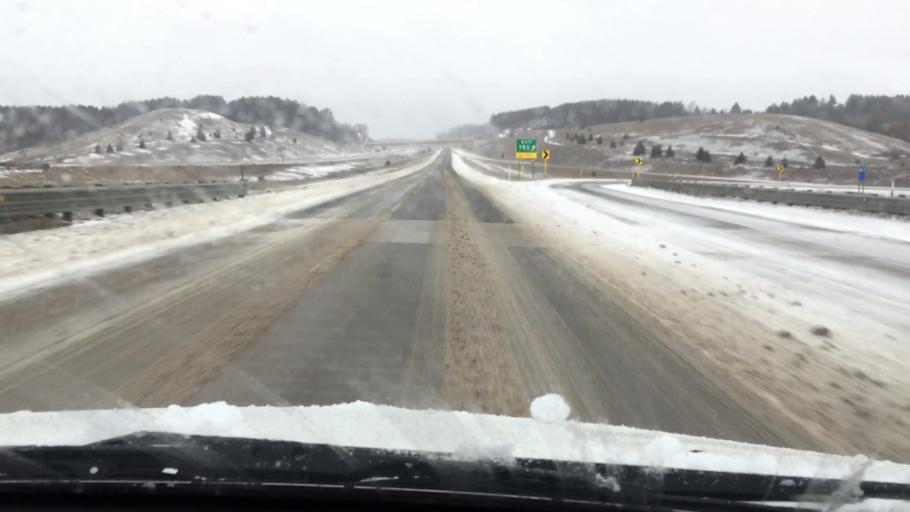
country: US
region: Michigan
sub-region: Wexford County
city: Manton
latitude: 44.4041
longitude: -85.3811
